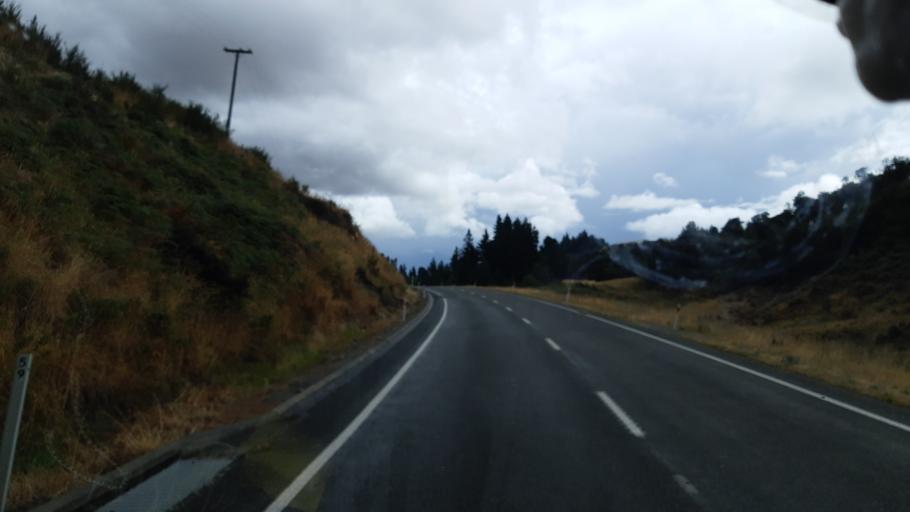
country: NZ
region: Canterbury
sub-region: Hurunui District
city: Amberley
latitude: -42.5957
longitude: 172.5311
